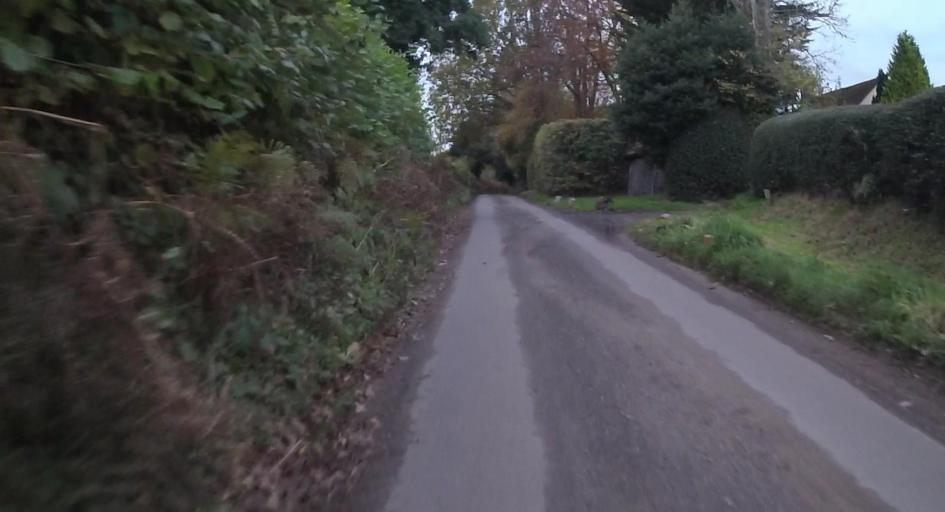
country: GB
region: England
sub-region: Hampshire
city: Lindford
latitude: 51.1333
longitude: -0.8196
